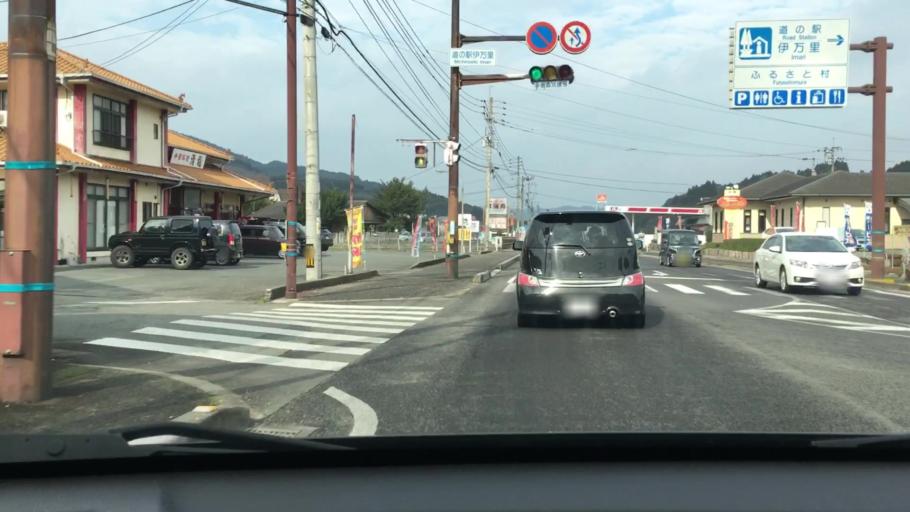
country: JP
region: Saga Prefecture
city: Imaricho-ko
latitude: 33.3135
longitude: 129.9286
